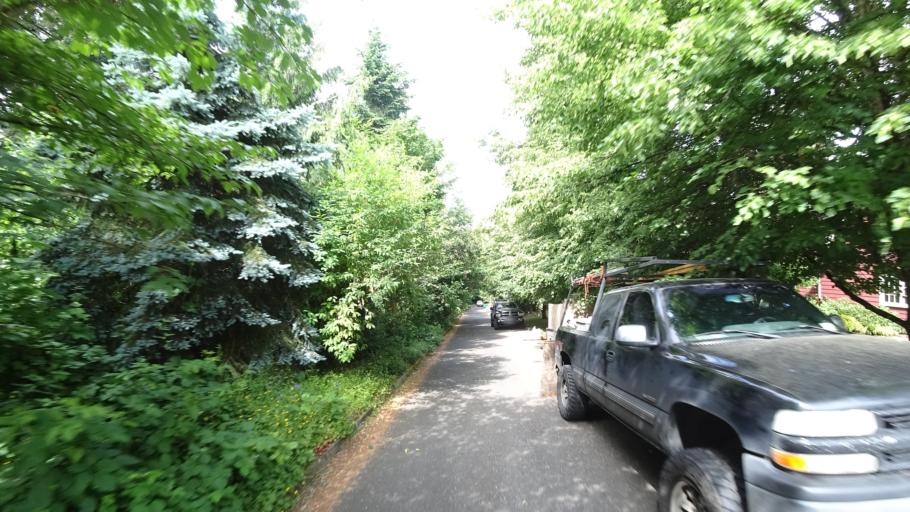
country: US
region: Oregon
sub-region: Clackamas County
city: Lake Oswego
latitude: 45.4543
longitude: -122.6873
